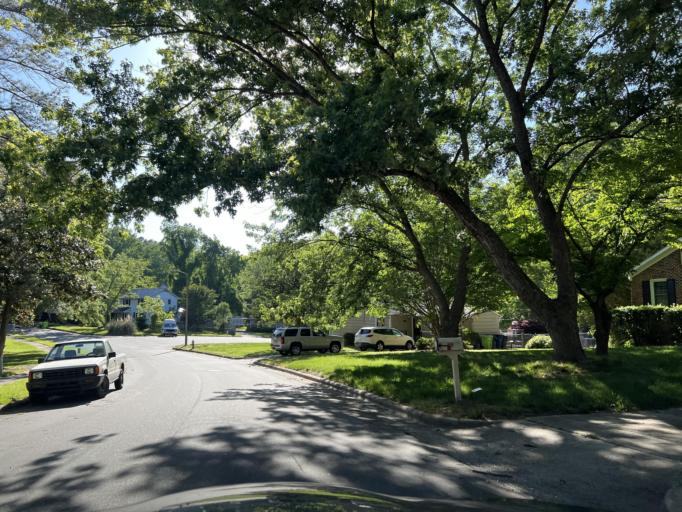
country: US
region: North Carolina
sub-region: Wake County
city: West Raleigh
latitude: 35.8647
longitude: -78.6433
